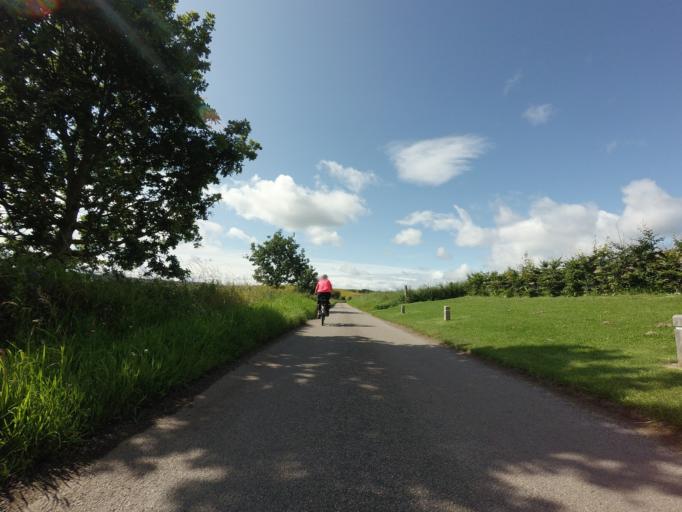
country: GB
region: Scotland
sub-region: Moray
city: Kinloss
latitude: 57.6464
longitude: -3.5150
